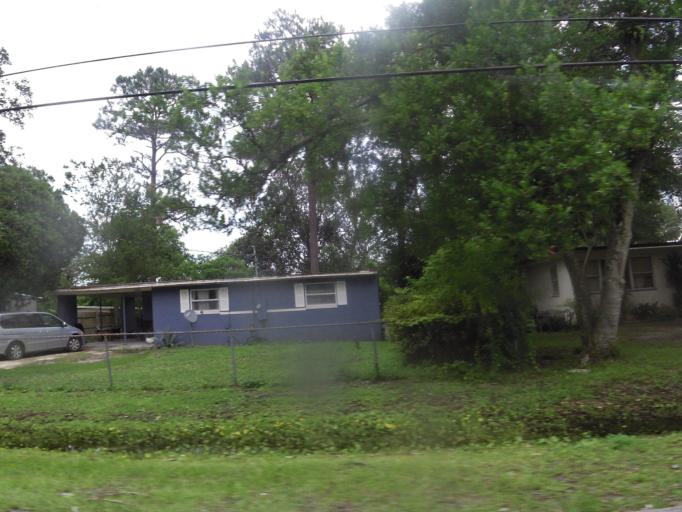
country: US
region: Florida
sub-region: Duval County
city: Jacksonville
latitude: 30.3177
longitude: -81.5310
